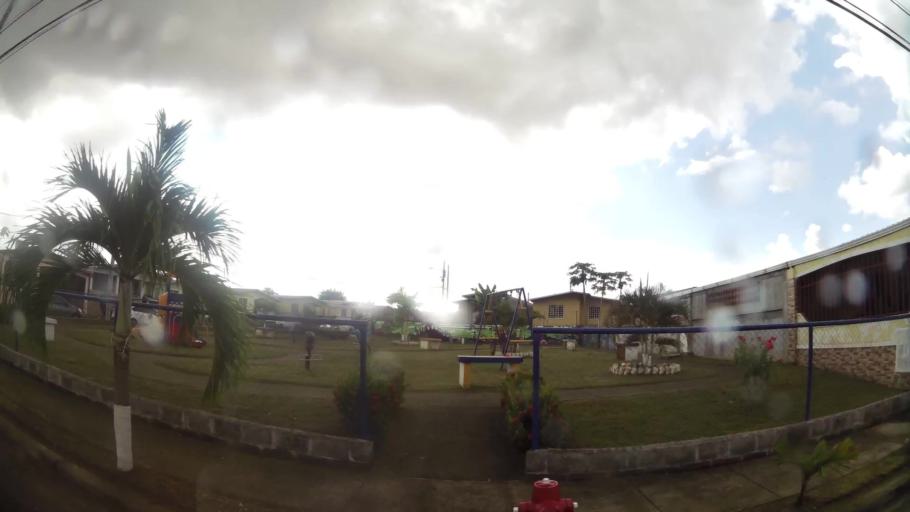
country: PA
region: Panama
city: Nuevo Arraijan
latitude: 8.9414
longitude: -79.7387
